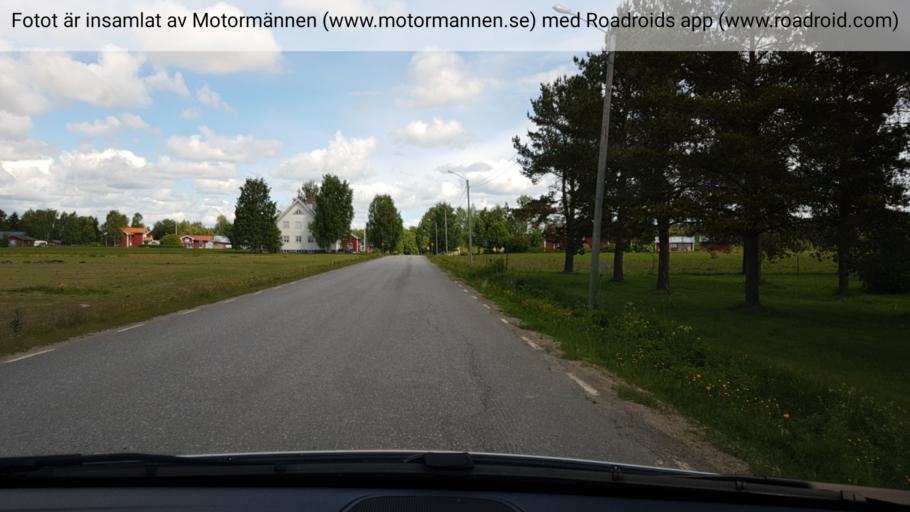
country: SE
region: Vaesterbotten
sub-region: Vannas Kommun
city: Vannasby
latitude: 63.9771
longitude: 19.8903
